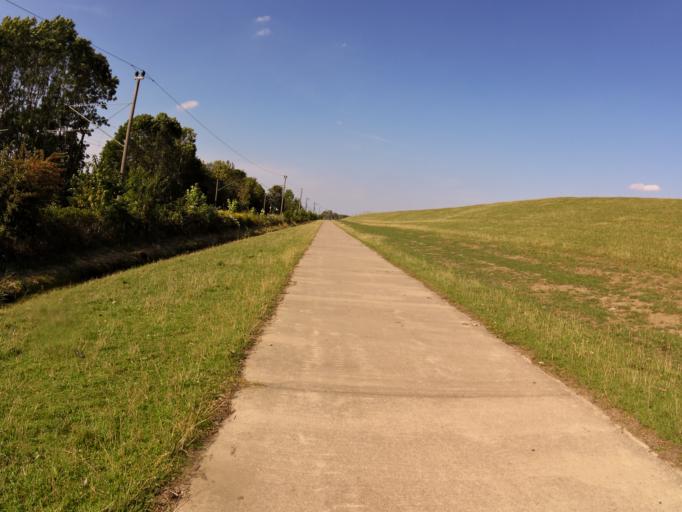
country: DE
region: Lower Saxony
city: Nordenham
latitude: 53.4455
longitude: 8.4763
